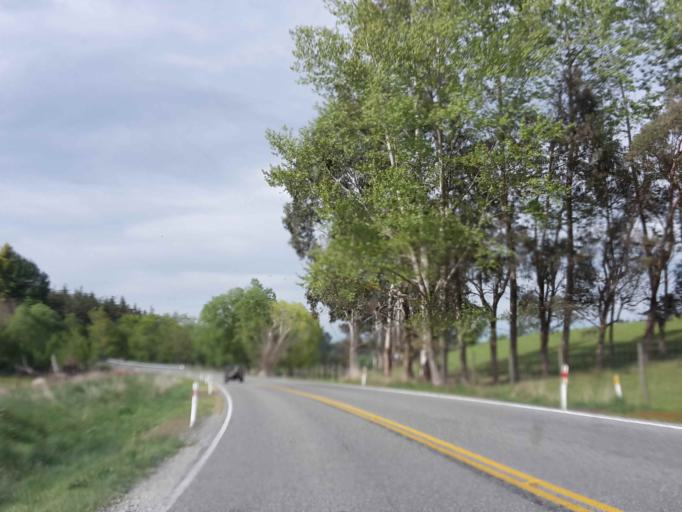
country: NZ
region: Canterbury
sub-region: Timaru District
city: Pleasant Point
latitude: -44.1173
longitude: 171.1325
